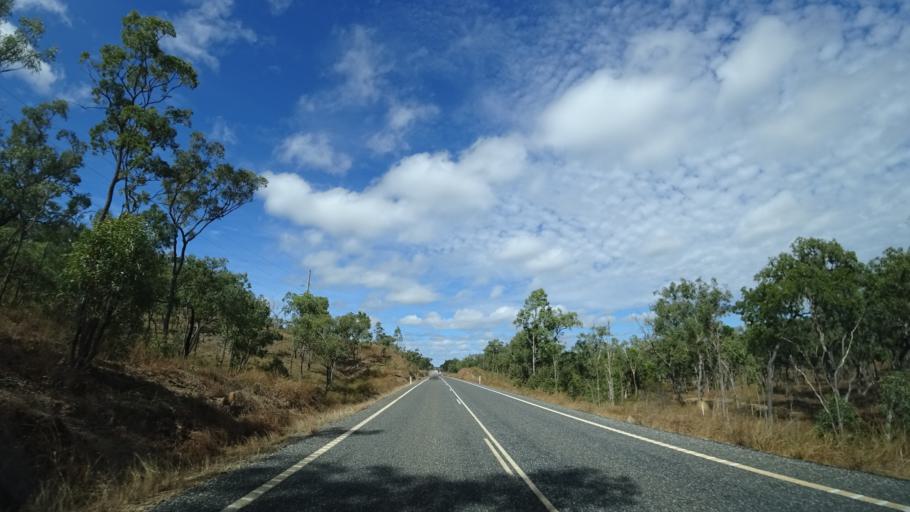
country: AU
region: Queensland
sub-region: Cairns
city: Port Douglas
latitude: -16.3093
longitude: 144.7174
